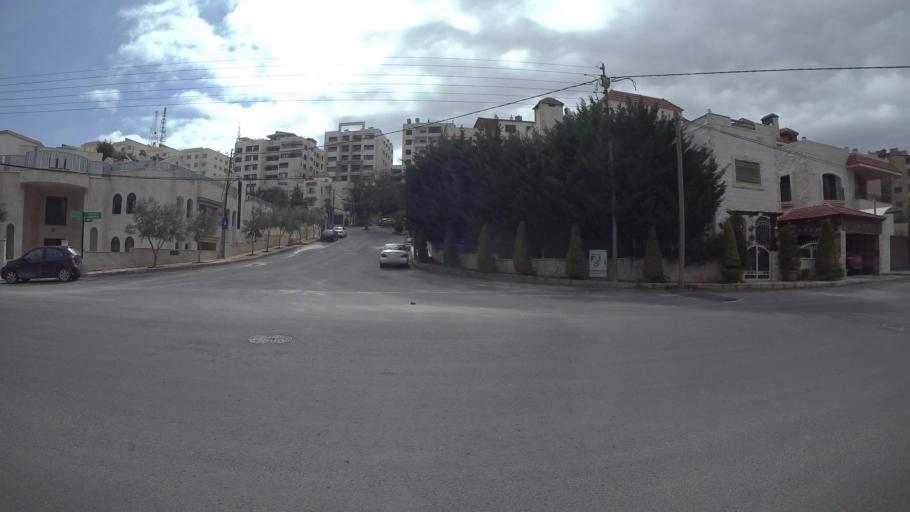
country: JO
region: Amman
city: Al Jubayhah
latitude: 32.0074
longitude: 35.8378
